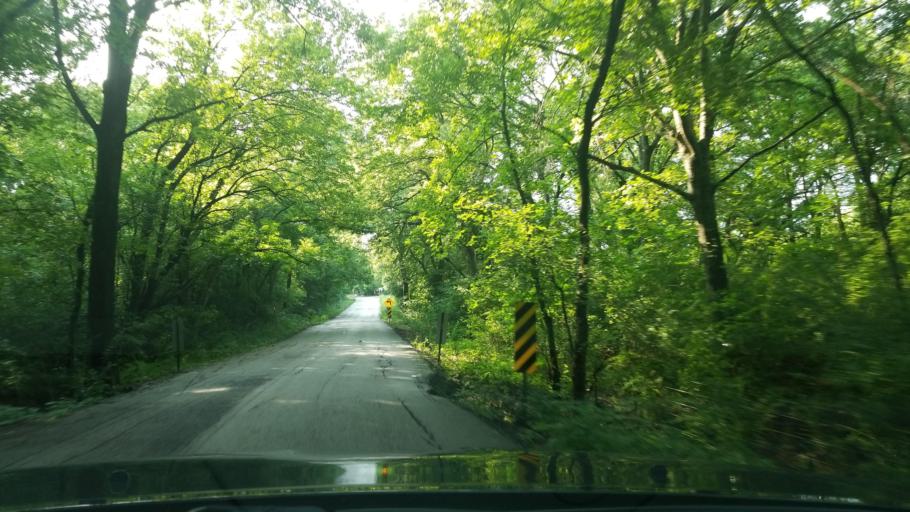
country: US
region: Texas
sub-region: Denton County
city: Cross Roads
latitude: 33.2571
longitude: -97.0617
